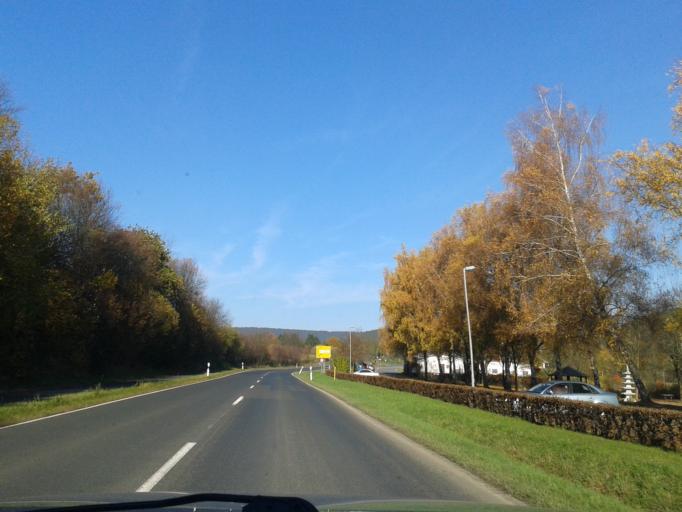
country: DE
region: Hesse
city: Dillenburg
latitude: 50.8373
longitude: 8.3365
